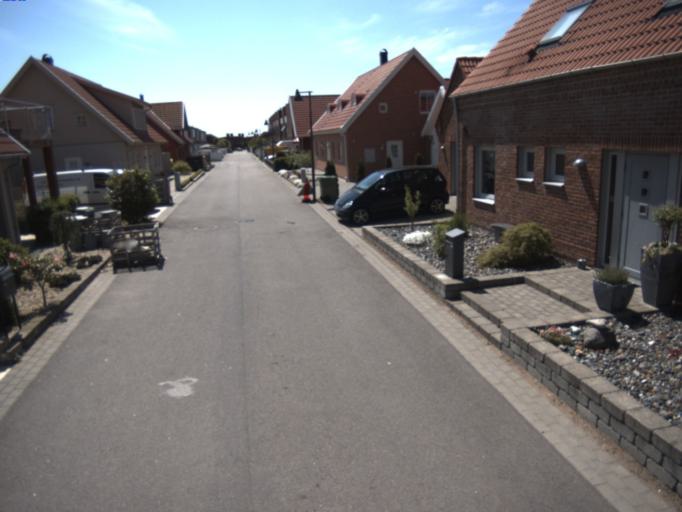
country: SE
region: Skane
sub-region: Helsingborg
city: Rydeback
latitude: 56.0078
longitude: 12.7536
